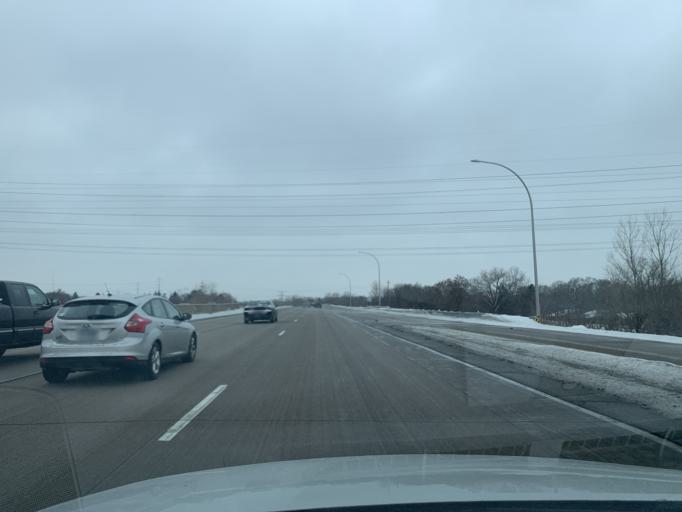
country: US
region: Minnesota
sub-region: Anoka County
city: Coon Rapids
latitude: 45.1403
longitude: -93.2868
